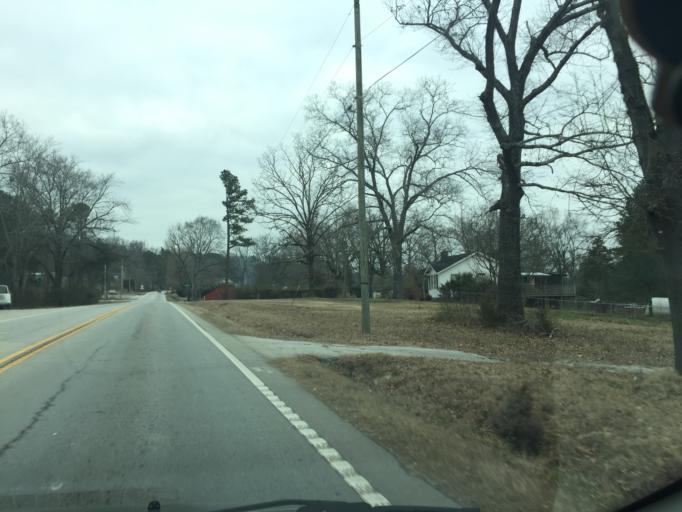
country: US
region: Georgia
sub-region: Catoosa County
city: Indian Springs
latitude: 34.9676
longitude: -85.1820
